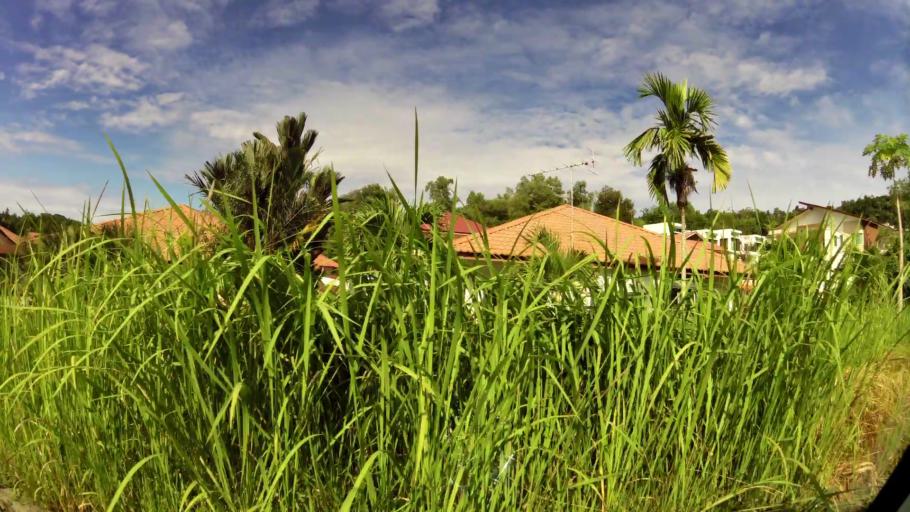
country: BN
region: Brunei and Muara
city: Bandar Seri Begawan
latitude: 4.9033
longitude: 114.9701
